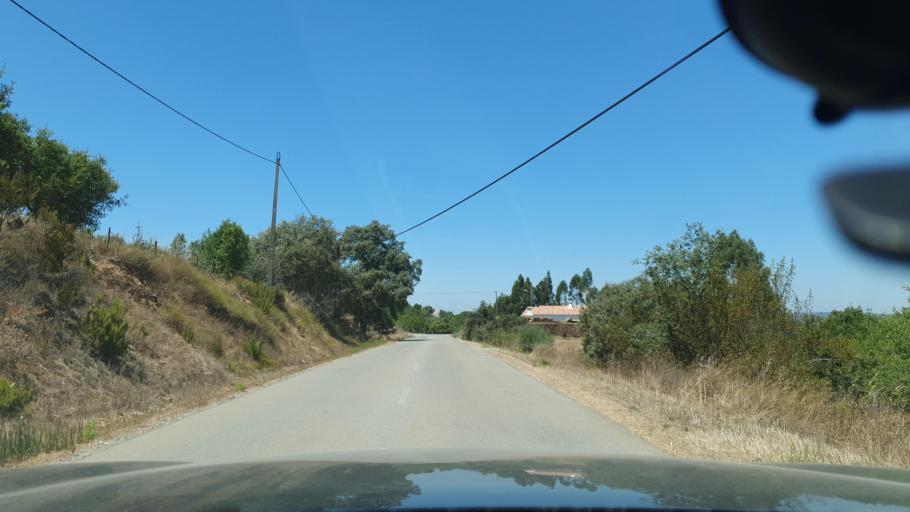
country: PT
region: Beja
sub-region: Odemira
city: Odemira
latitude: 37.5511
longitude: -8.4263
